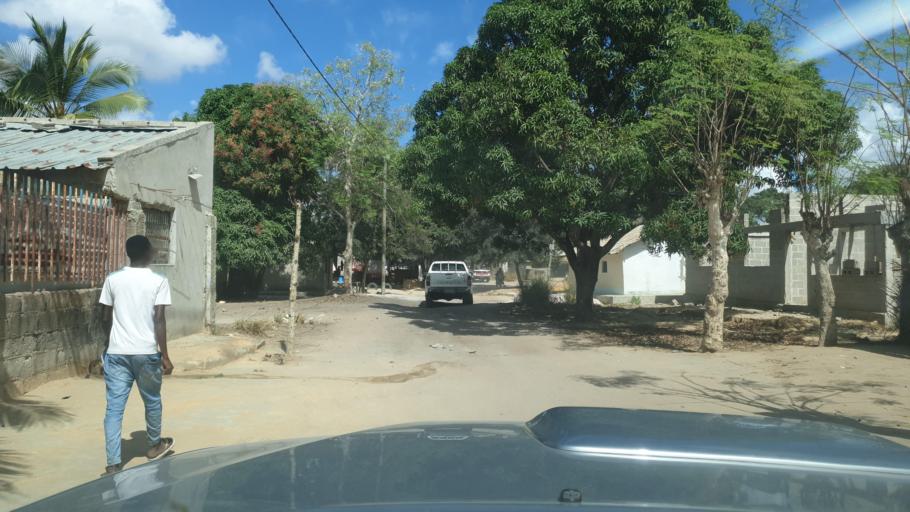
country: MZ
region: Nampula
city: Nacala
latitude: -14.5697
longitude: 40.6993
